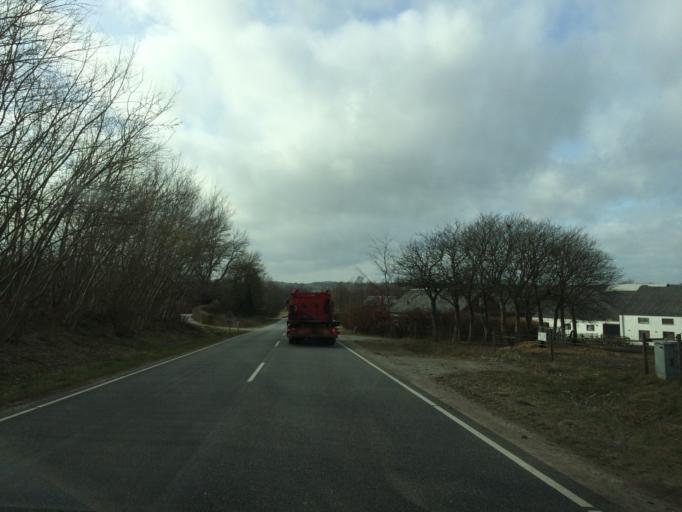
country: DK
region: Central Jutland
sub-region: Randers Kommune
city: Langa
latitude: 56.4859
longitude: 9.8676
